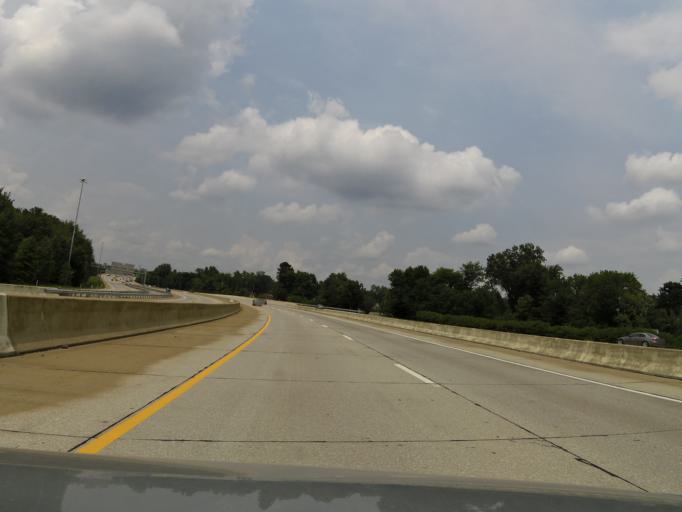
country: US
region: Kentucky
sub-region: Jefferson County
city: Beechwood Village
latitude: 38.2523
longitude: -85.6190
